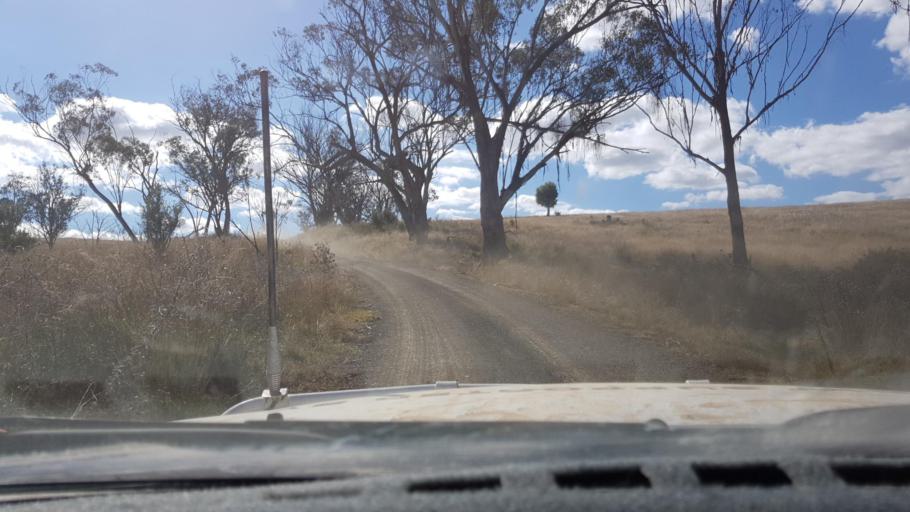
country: AU
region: New South Wales
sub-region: Tamworth Municipality
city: Manilla
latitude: -30.4715
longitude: 150.7751
